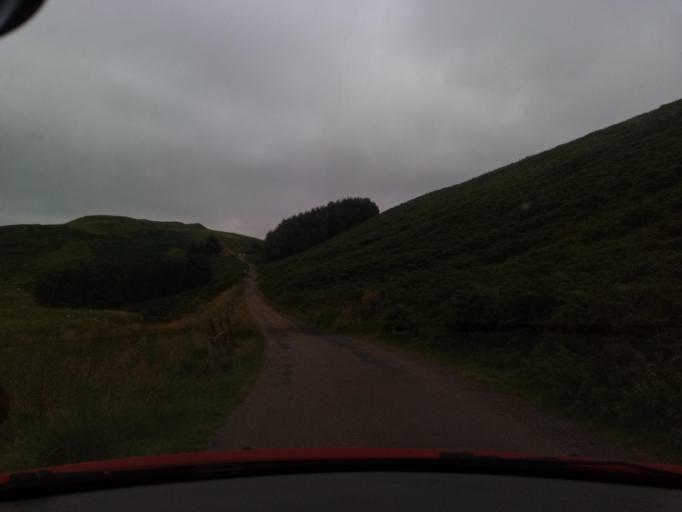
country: GB
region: England
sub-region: Northumberland
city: Rochester
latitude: 55.3718
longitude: -2.2156
